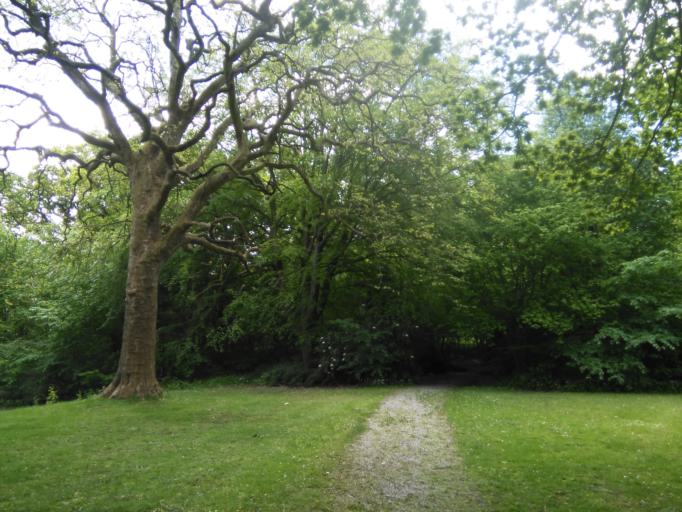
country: DK
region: Central Jutland
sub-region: Arhus Kommune
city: Arhus
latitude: 56.1861
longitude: 10.2353
